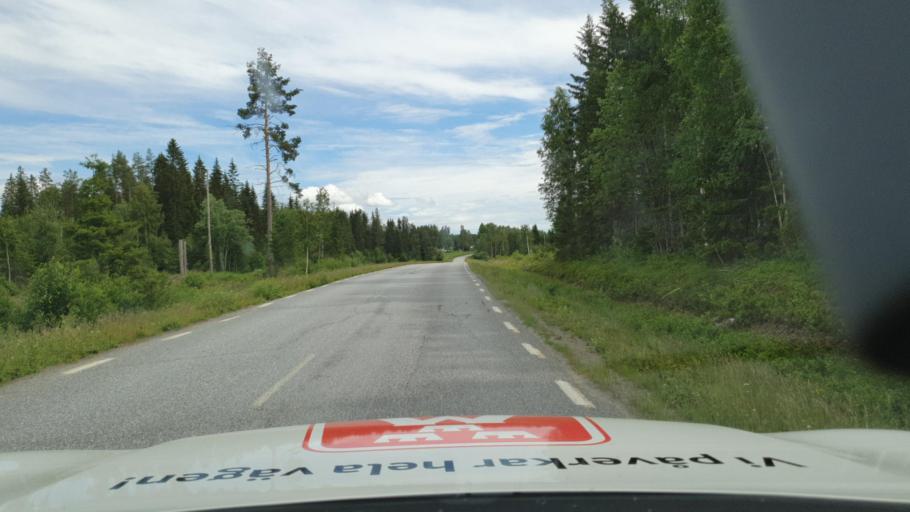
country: SE
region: Vaesterbotten
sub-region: Skelleftea Kommun
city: Soedra Bergsbyn
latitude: 64.5140
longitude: 20.9932
